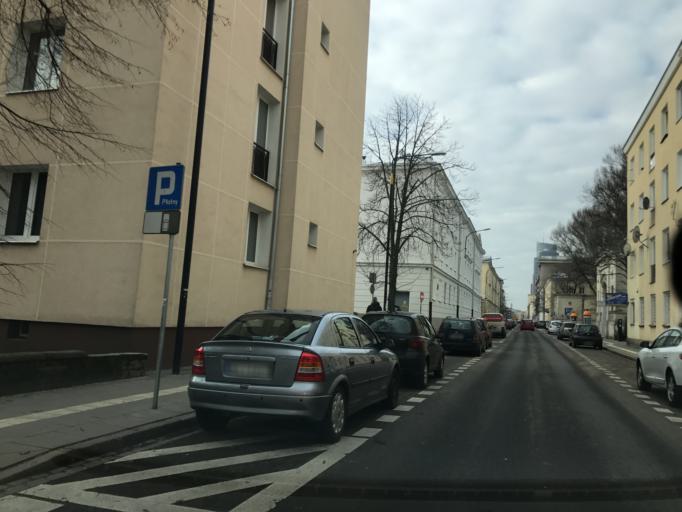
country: PL
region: Masovian Voivodeship
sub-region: Warszawa
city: Wola
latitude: 52.2409
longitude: 20.9996
